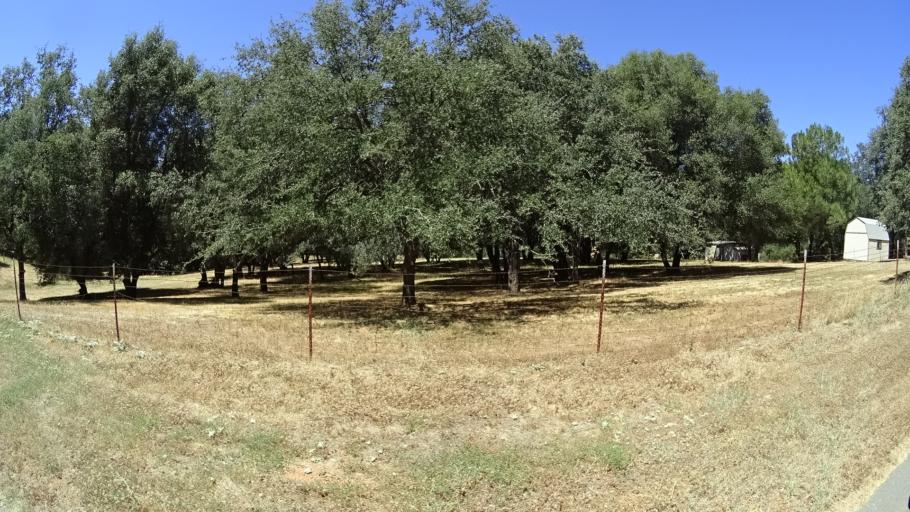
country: US
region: California
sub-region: Amador County
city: Pine Grove
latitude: 38.3418
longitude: -120.6122
